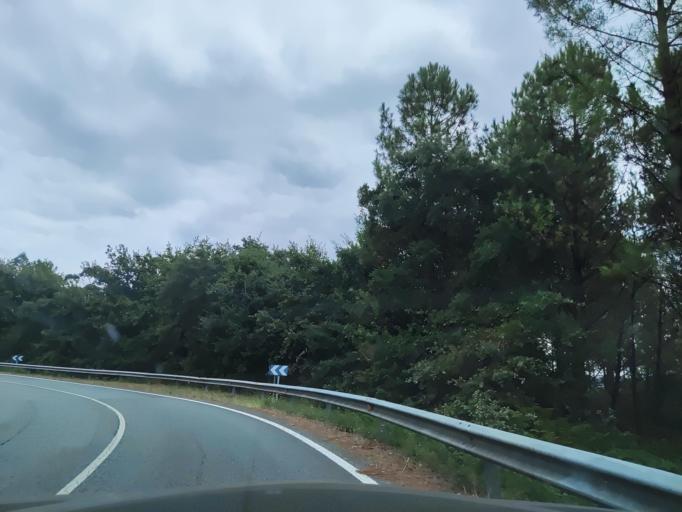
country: ES
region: Galicia
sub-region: Provincia da Coruna
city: Padron
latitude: 42.7467
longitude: -8.6156
